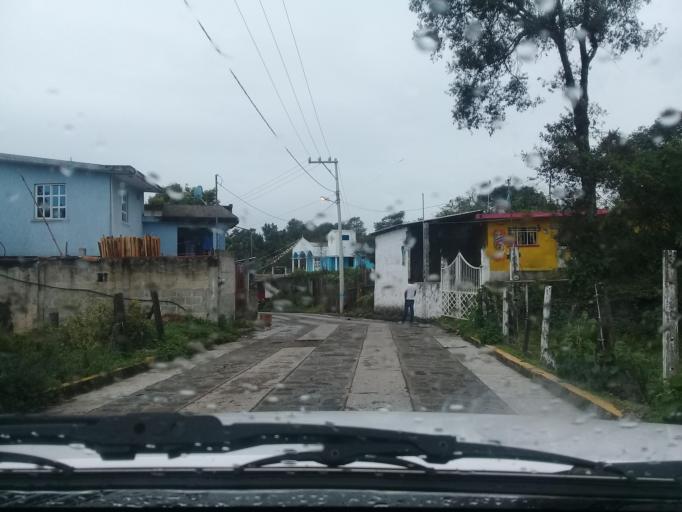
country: MX
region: Veracruz
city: Rafael Lucio
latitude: 19.6149
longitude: -96.9925
